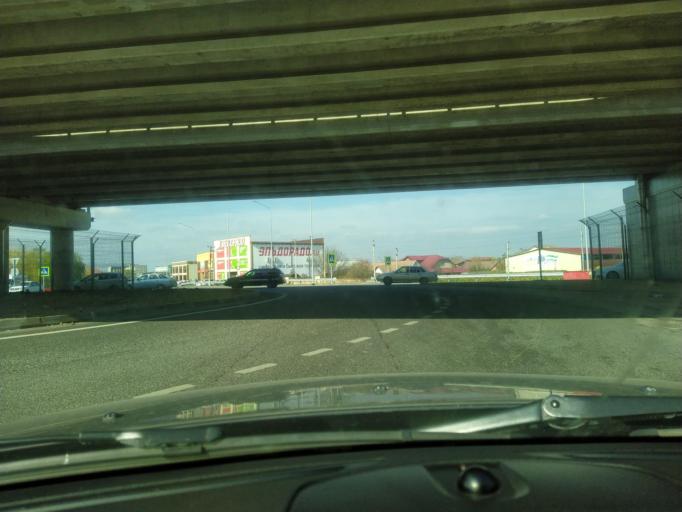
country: RU
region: Ingushetiya
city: Magas
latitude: 43.1952
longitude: 44.7614
